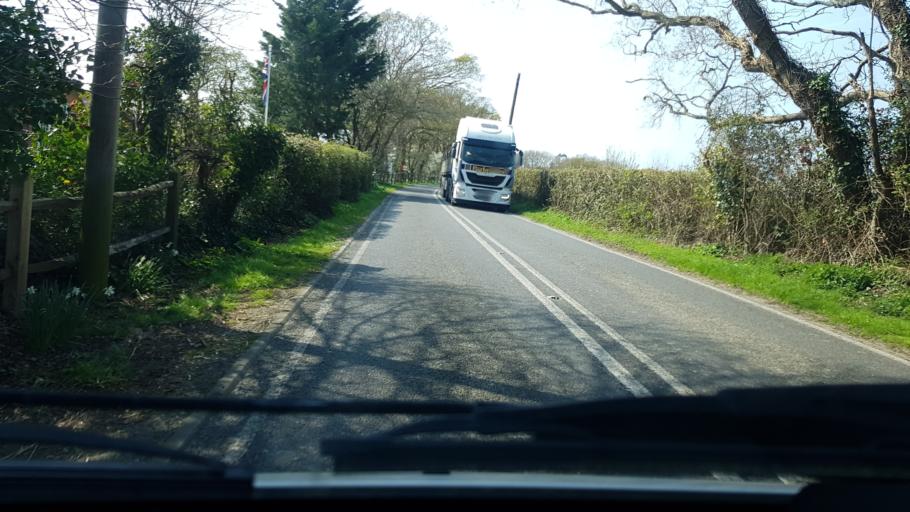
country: GB
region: England
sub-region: West Sussex
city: East Wittering
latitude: 50.7873
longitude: -0.8745
